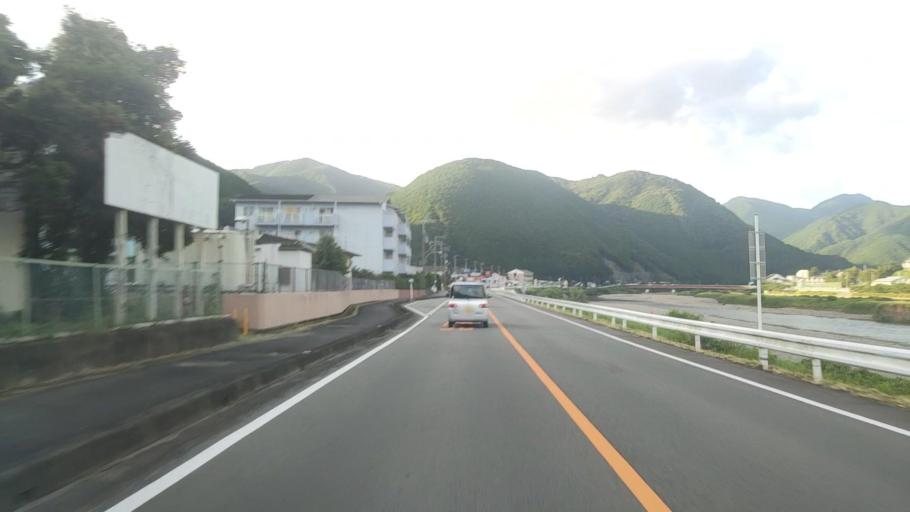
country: JP
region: Wakayama
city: Tanabe
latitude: 33.7255
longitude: 135.4820
